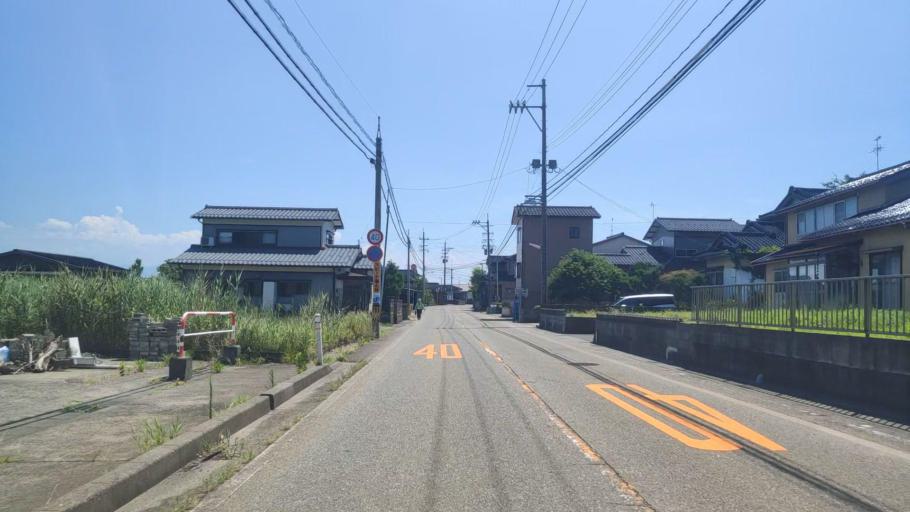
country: JP
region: Ishikawa
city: Kanazawa-shi
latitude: 36.6635
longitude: 136.6570
